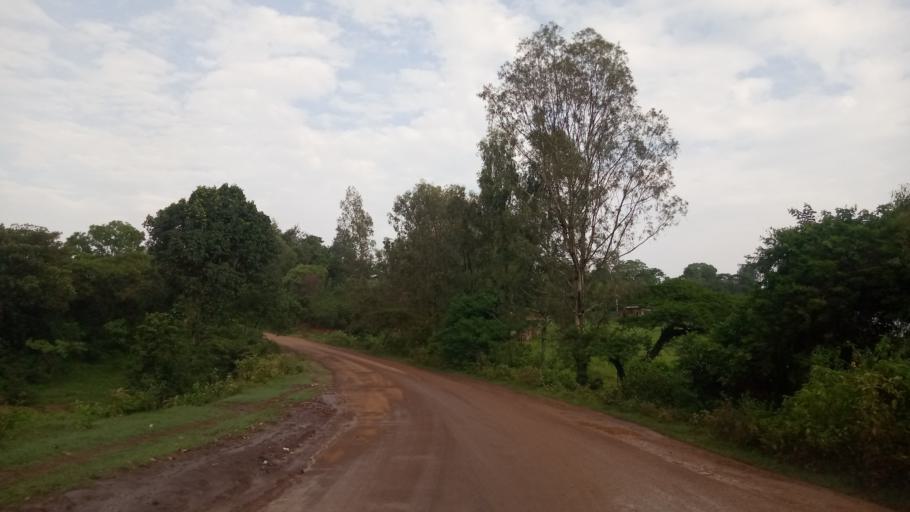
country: ET
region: Oromiya
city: Agaro
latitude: 7.8369
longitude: 36.6763
